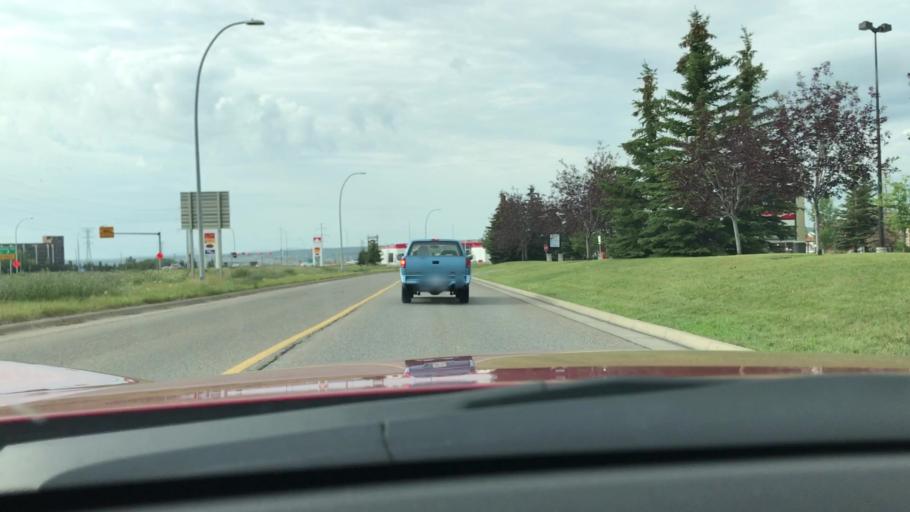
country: CA
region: Alberta
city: Calgary
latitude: 51.0210
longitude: -114.1665
